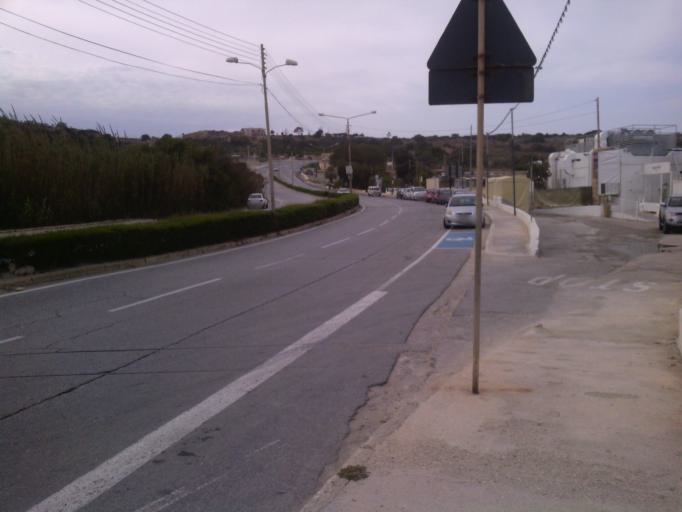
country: MT
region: Il-Mellieha
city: Mellieha
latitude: 35.9718
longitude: 14.3496
